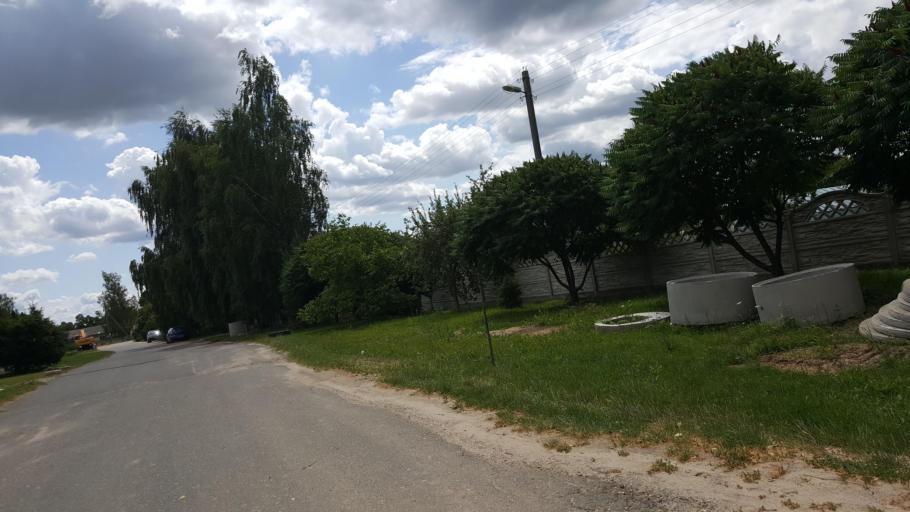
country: BY
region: Brest
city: Kamyanyets
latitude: 52.3977
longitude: 23.8352
